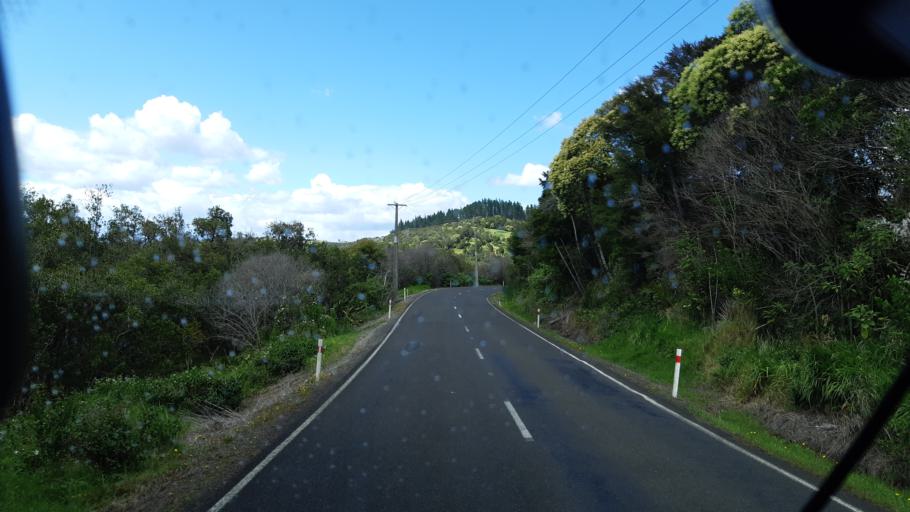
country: NZ
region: Northland
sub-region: Far North District
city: Taipa
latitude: -35.2703
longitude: 173.5228
